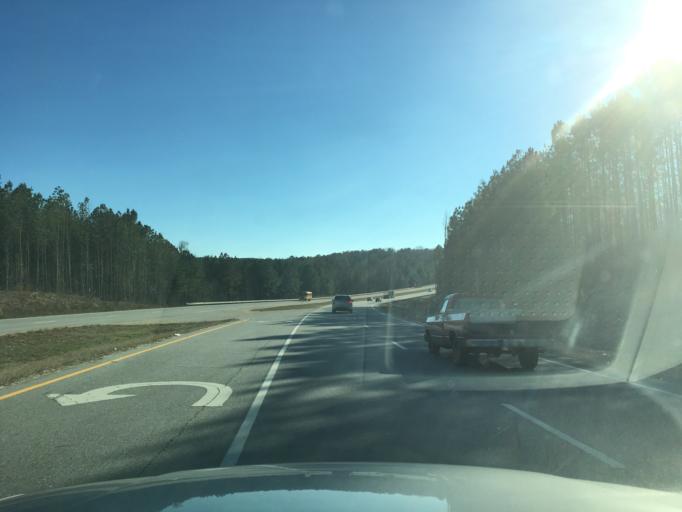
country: US
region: Georgia
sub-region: Carroll County
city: Carrollton
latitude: 33.4507
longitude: -85.1246
